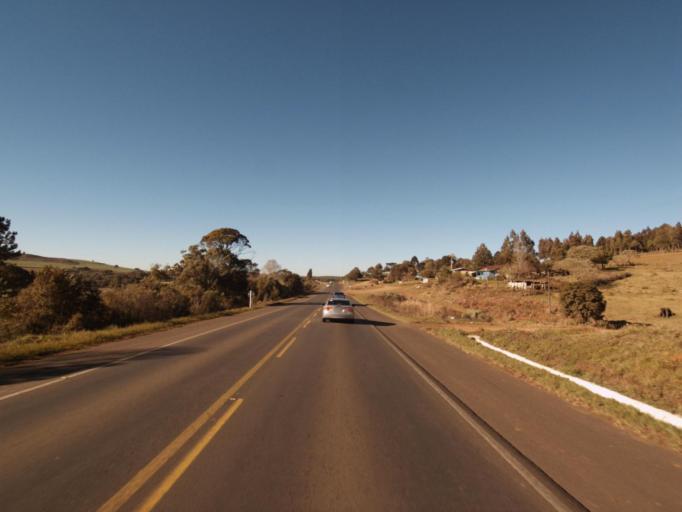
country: BR
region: Santa Catarina
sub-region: Concordia
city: Concordia
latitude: -26.9034
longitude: -51.9716
